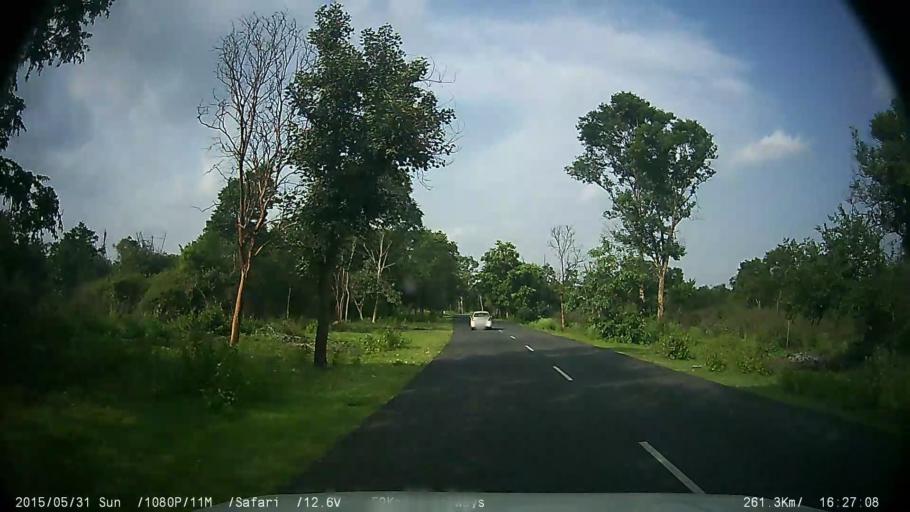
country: IN
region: Karnataka
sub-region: Chamrajnagar
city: Gundlupet
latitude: 11.7660
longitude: 76.5326
